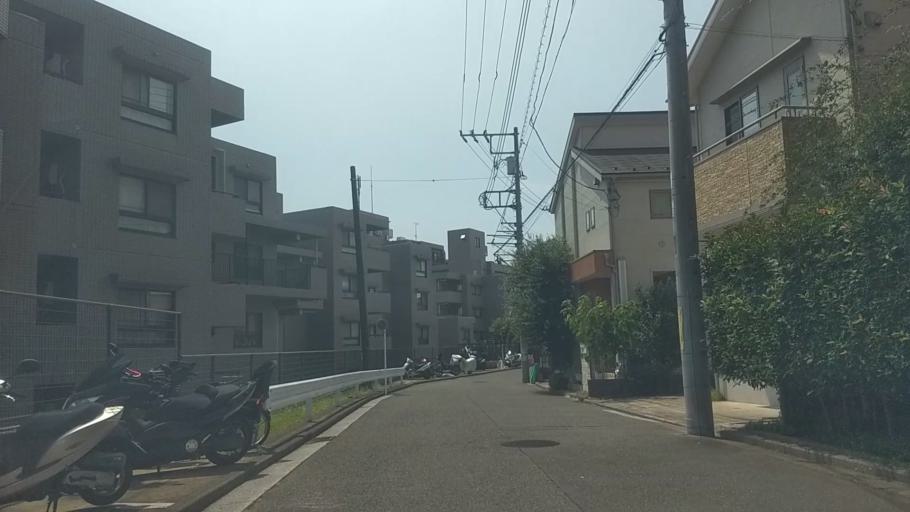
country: JP
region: Kanagawa
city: Yokohama
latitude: 35.4958
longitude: 139.6579
